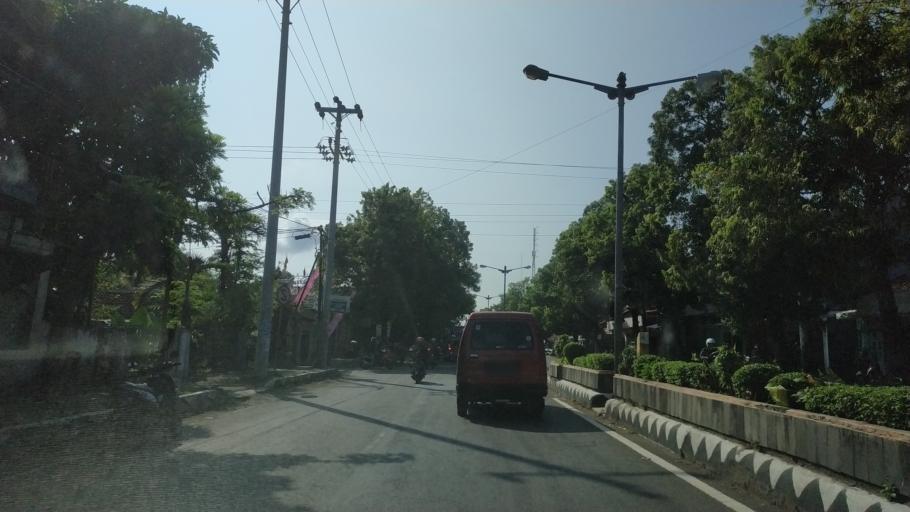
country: ID
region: Central Java
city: Petarukan
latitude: -6.8940
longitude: 109.4147
